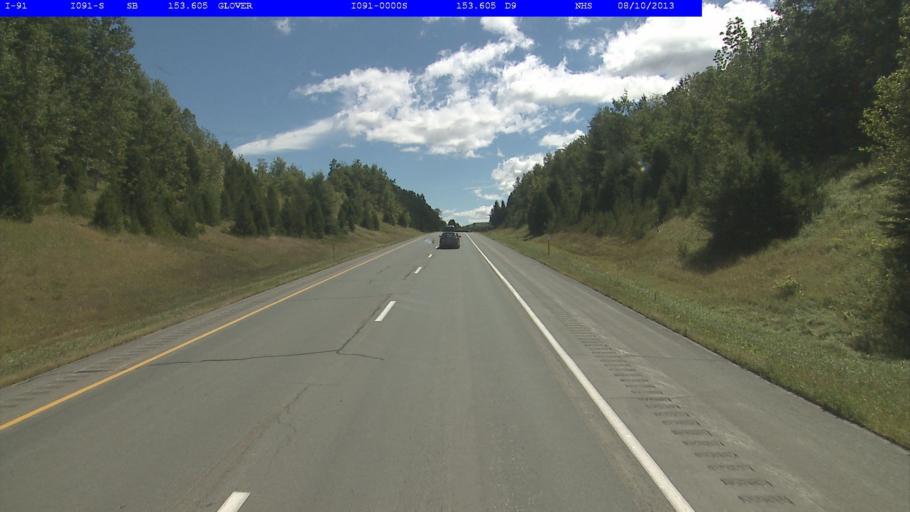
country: US
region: Vermont
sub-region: Orleans County
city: Newport
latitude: 44.7083
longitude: -72.1622
